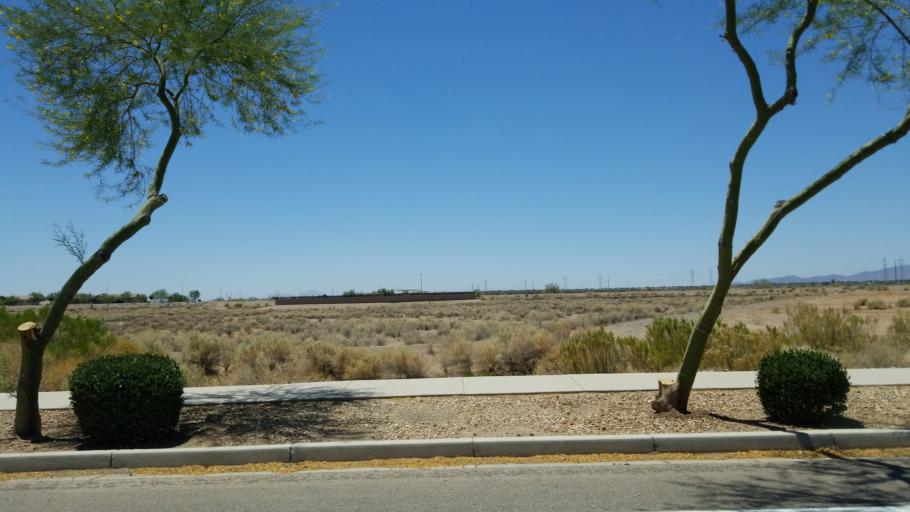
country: US
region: Arizona
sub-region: Maricopa County
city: Litchfield Park
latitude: 33.5108
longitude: -112.2998
